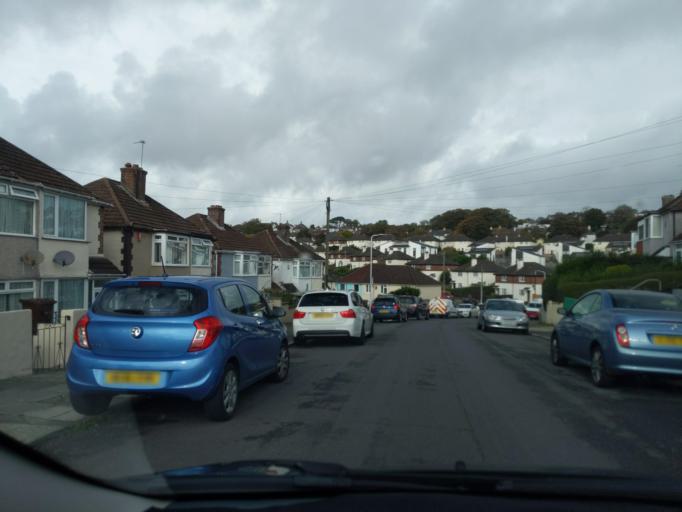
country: GB
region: England
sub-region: Cornwall
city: Torpoint
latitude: 50.4035
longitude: -4.1811
